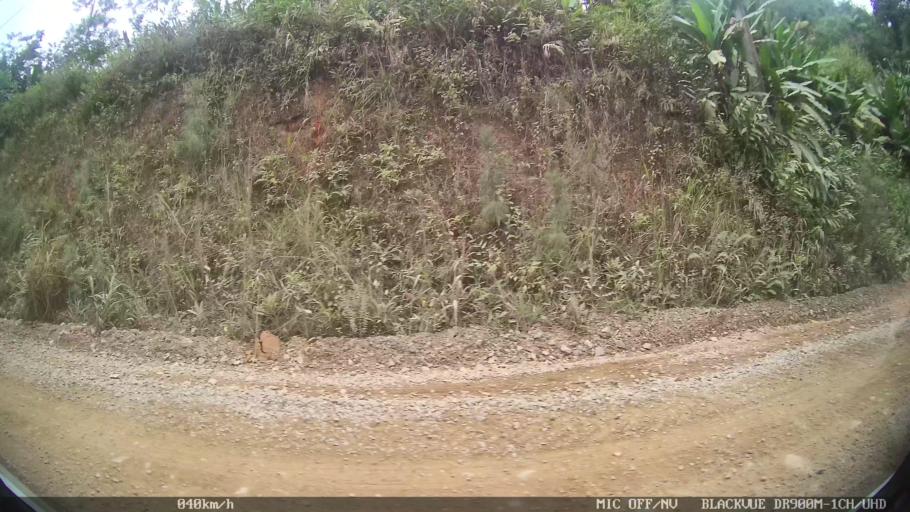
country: BR
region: Santa Catarina
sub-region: Joinville
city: Joinville
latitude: -26.2447
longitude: -48.9254
